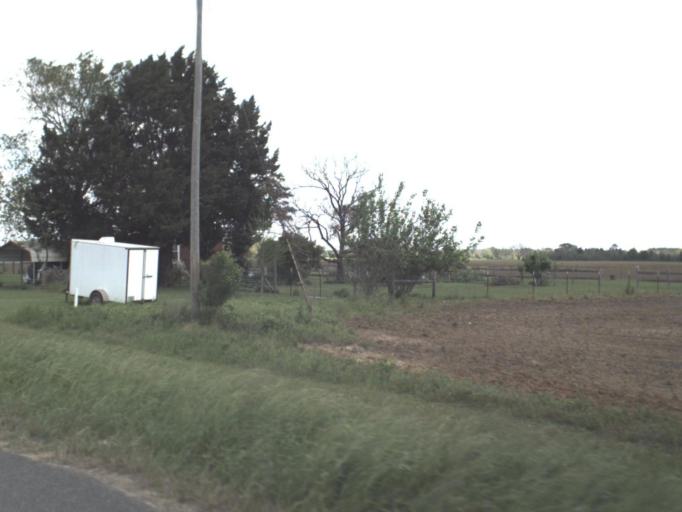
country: US
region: Florida
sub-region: Okaloosa County
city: Crestview
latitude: 30.8242
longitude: -86.6759
